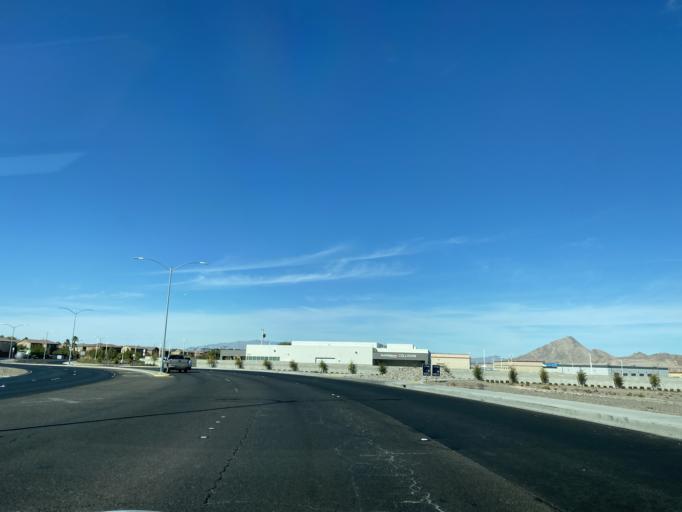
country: US
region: Nevada
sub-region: Clark County
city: Henderson
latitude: 36.0652
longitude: -115.0271
